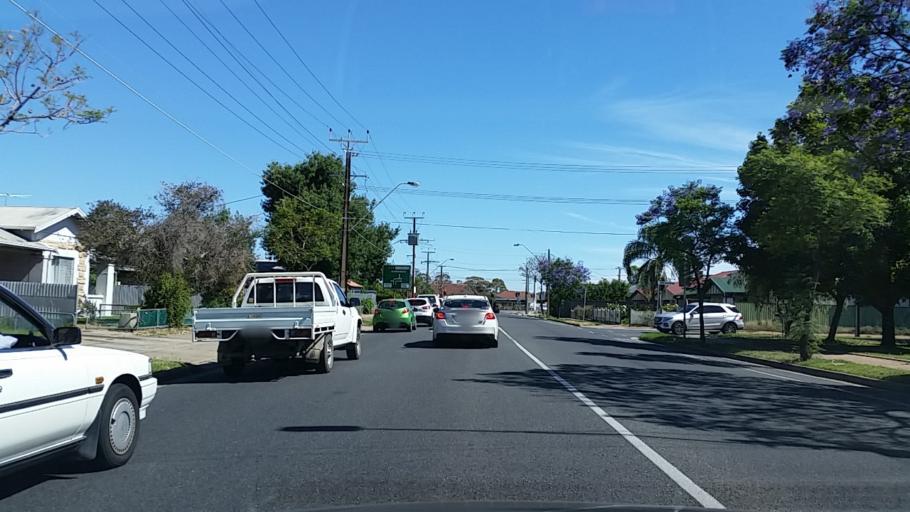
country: AU
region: South Australia
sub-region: Charles Sturt
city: Allenby Gardens
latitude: -34.9029
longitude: 138.5520
